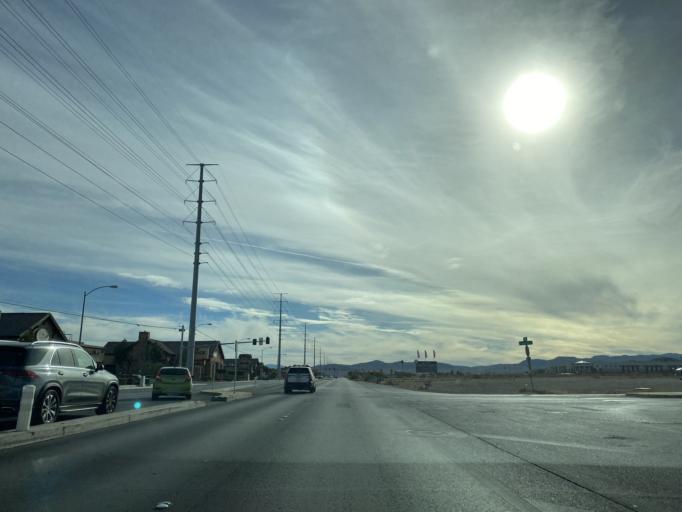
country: US
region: Nevada
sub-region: Clark County
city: Enterprise
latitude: 36.0380
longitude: -115.2435
